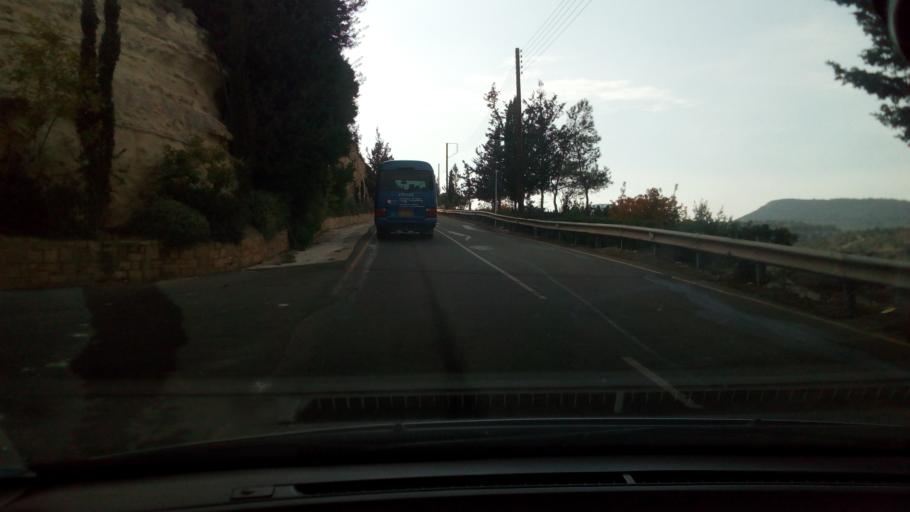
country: CY
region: Pafos
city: Polis
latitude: 35.0344
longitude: 32.3645
